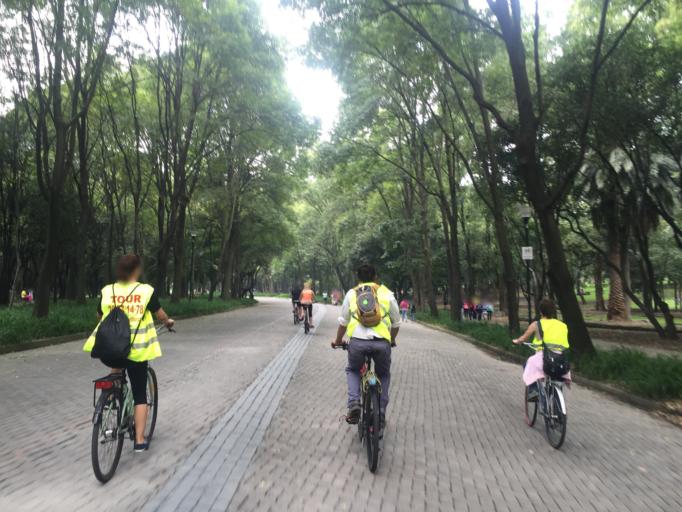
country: MX
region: Mexico City
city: Polanco
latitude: 19.4175
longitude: -99.1816
